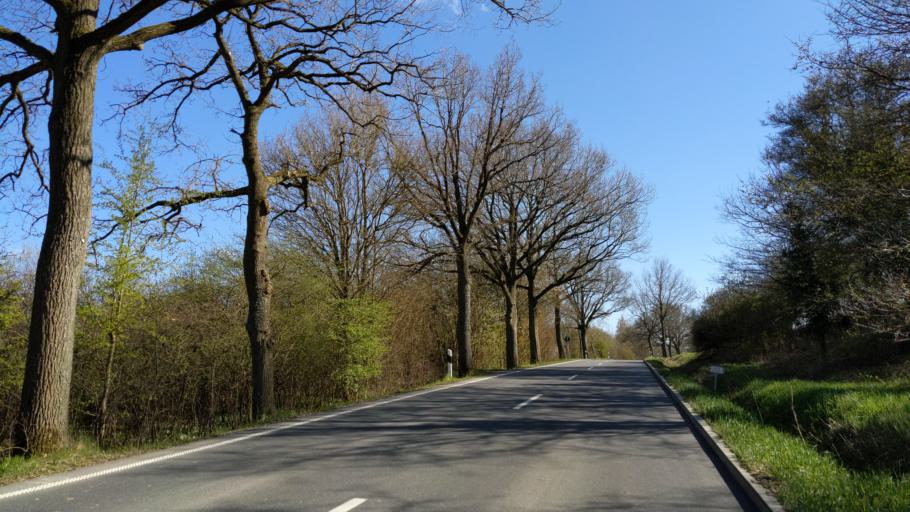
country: DE
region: Schleswig-Holstein
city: Eutin
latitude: 54.0881
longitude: 10.6193
